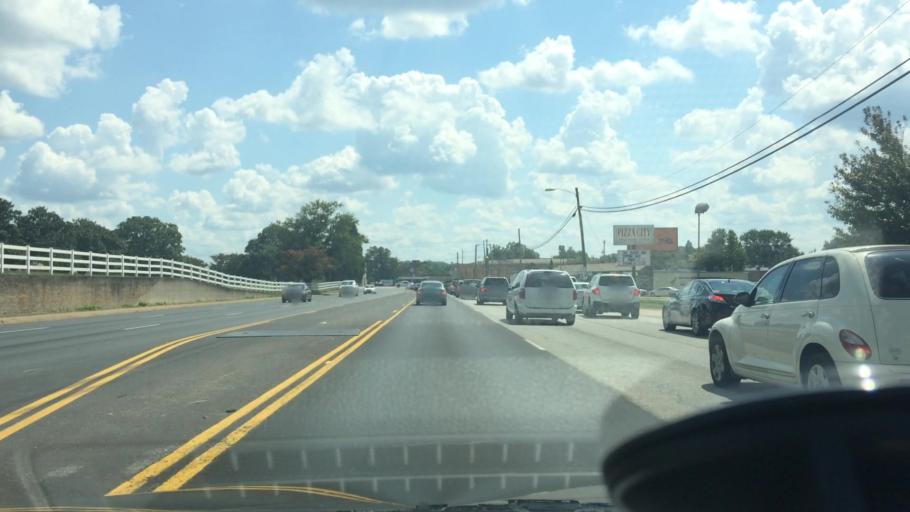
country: US
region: South Carolina
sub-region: Greenville County
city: Wade Hampton
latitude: 34.8799
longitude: -82.3637
